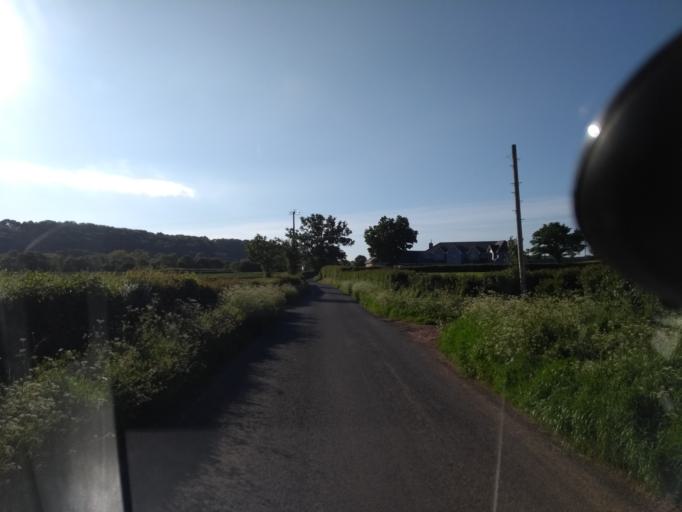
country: GB
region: England
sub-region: Somerset
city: Creech Saint Michael
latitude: 50.9980
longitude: -3.0595
